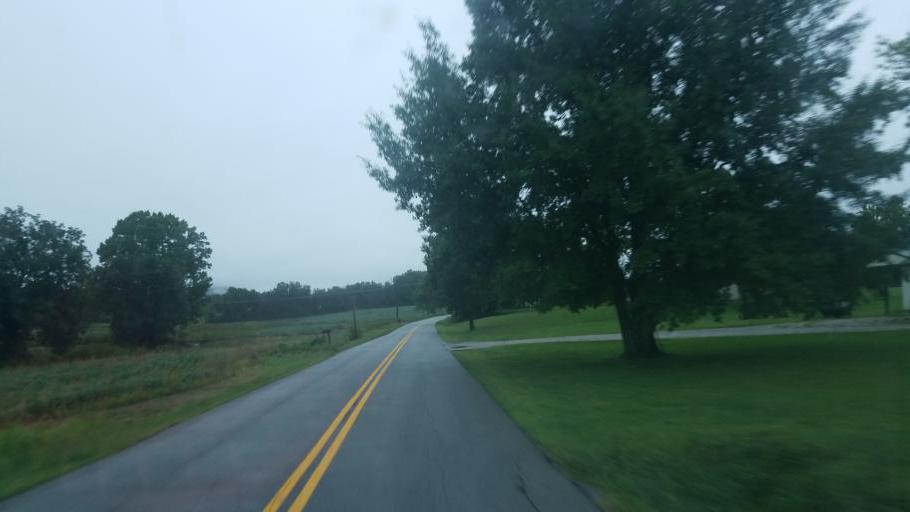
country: US
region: Kentucky
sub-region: Fleming County
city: Flemingsburg
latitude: 38.4042
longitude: -83.6018
